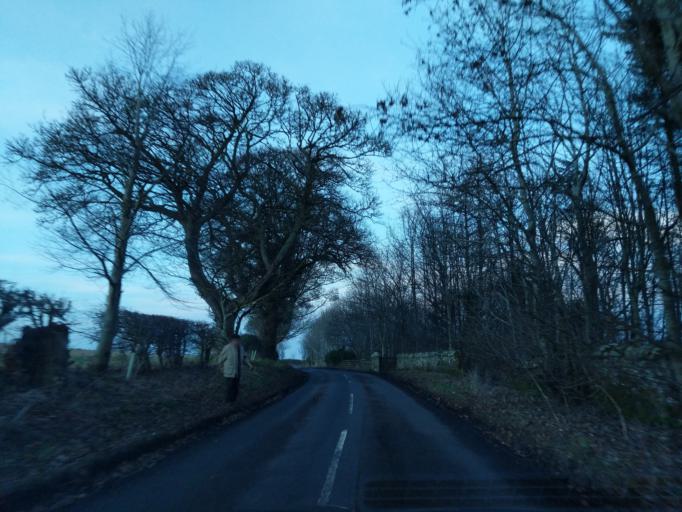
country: GB
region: Scotland
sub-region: Midlothian
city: Gorebridge
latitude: 55.8268
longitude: -3.0839
